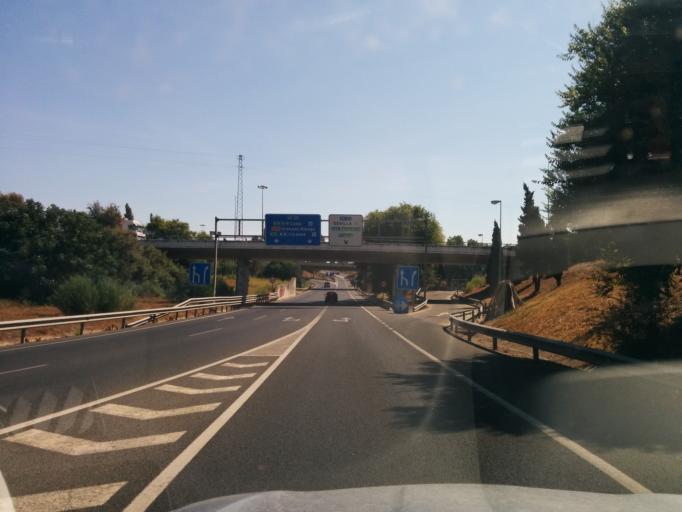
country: ES
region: Andalusia
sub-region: Provincia de Sevilla
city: San Juan de Aznalfarache
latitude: 37.3735
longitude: -6.0157
